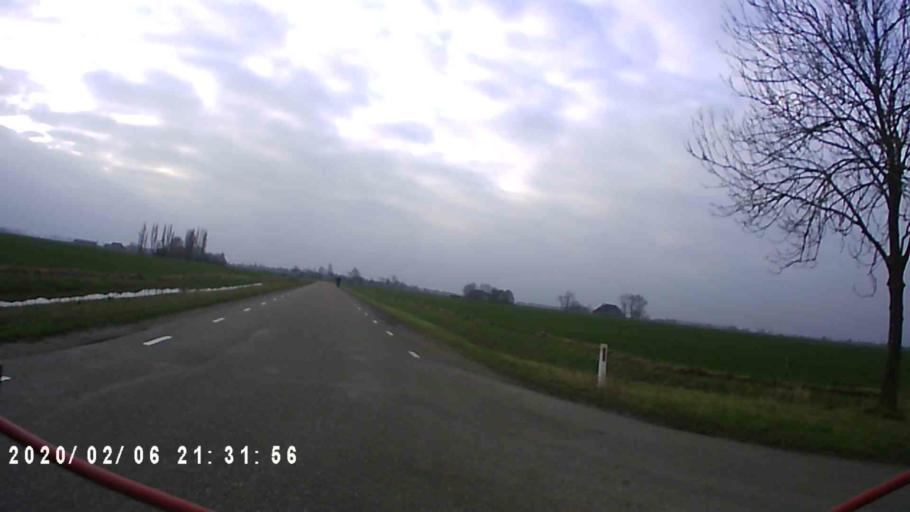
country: NL
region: Groningen
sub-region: Gemeente Zuidhorn
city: Noordhorn
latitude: 53.2814
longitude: 6.3888
